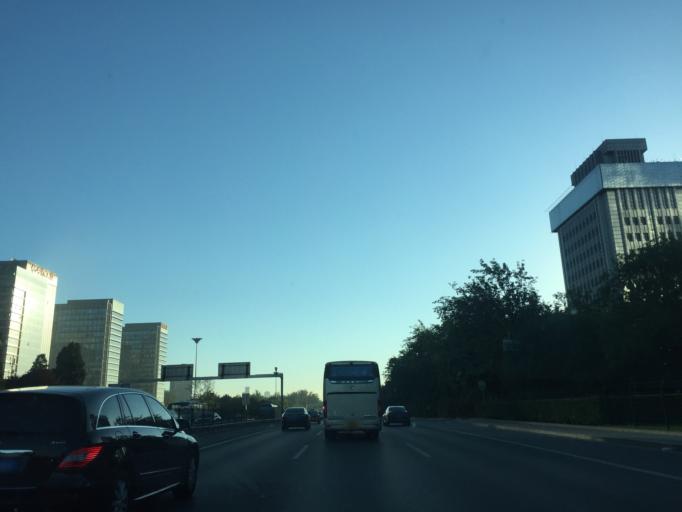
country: CN
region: Beijing
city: Chaowai
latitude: 39.9573
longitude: 116.4492
